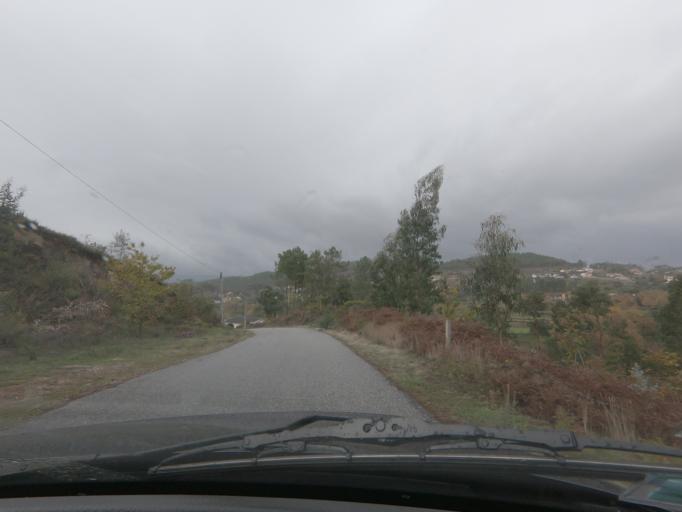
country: PT
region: Vila Real
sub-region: Mondim de Basto
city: Mondim de Basto
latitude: 41.3739
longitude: -7.9454
